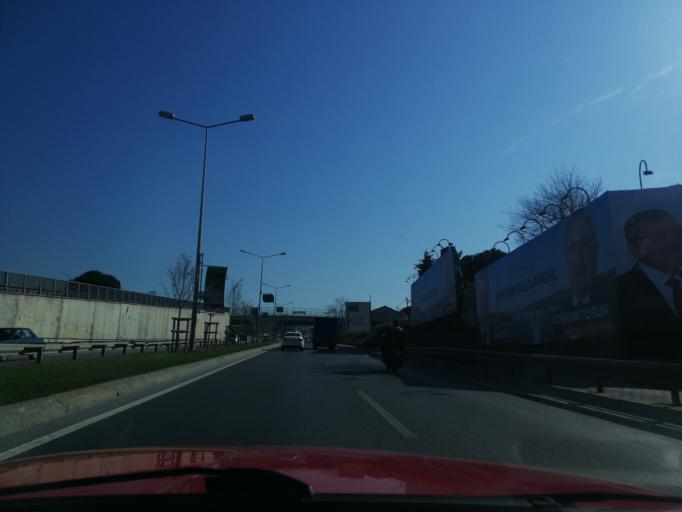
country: TR
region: Istanbul
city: Umraniye
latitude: 41.1013
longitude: 29.0974
